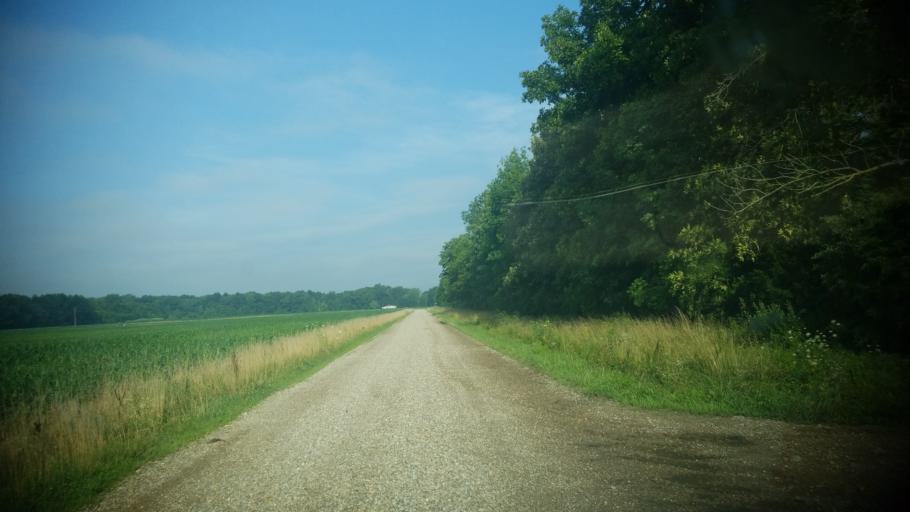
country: US
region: Illinois
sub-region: Clay County
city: Flora
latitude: 38.6021
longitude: -88.3602
